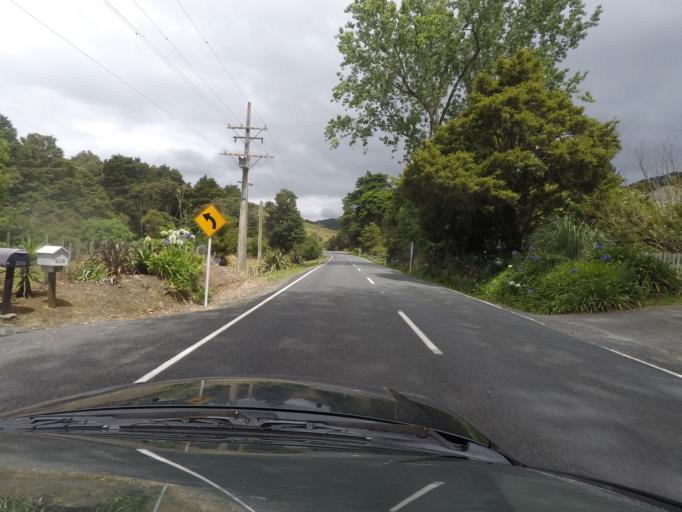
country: NZ
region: Auckland
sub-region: Auckland
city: Wellsford
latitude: -36.2928
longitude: 174.6148
